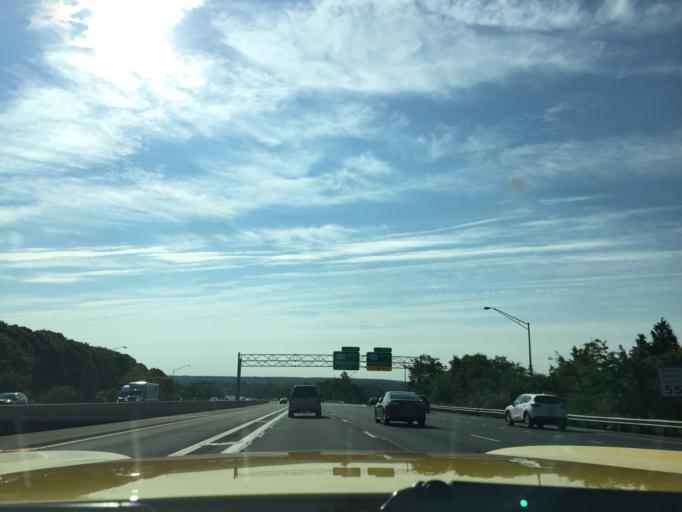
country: US
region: New York
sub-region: Suffolk County
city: Melville
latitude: 40.7827
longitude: -73.4346
